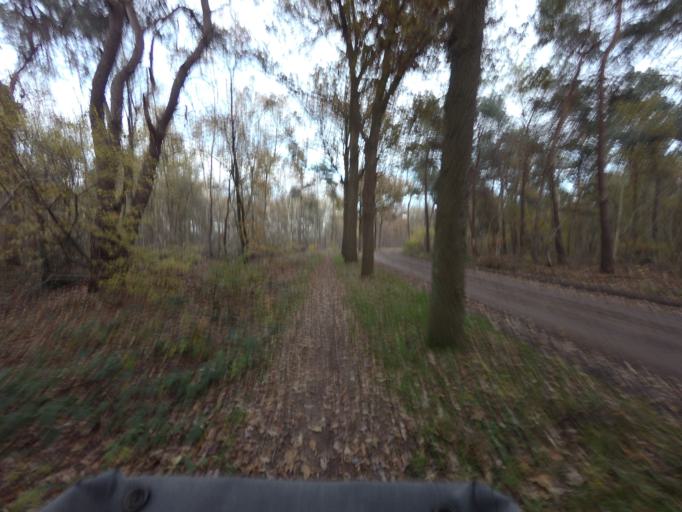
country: NL
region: North Brabant
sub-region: Gemeente Breda
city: Breda
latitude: 51.5098
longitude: 4.7959
